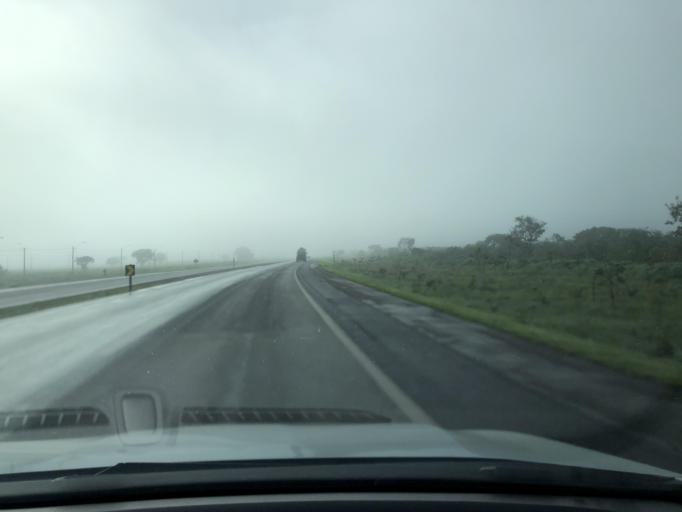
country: BR
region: Goias
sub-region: Luziania
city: Luziania
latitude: -16.2797
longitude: -47.8603
